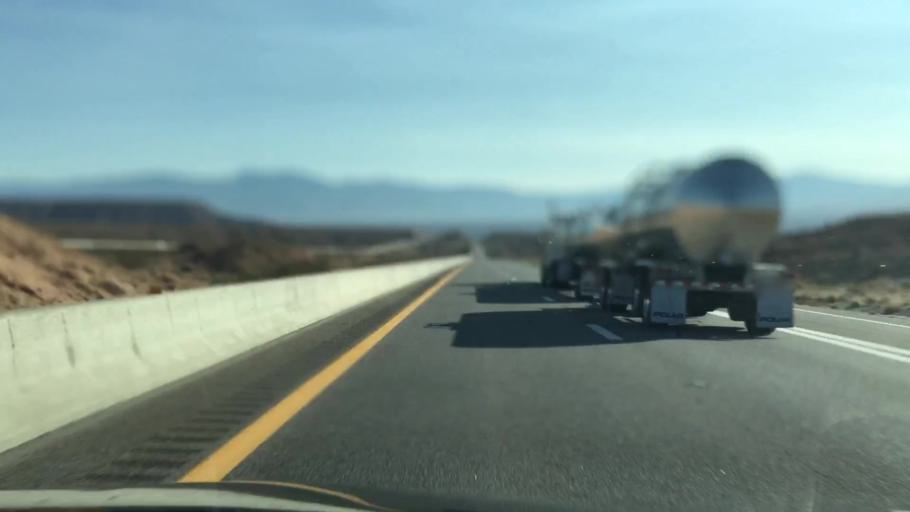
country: US
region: Nevada
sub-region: Clark County
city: Bunkerville
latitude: 36.7695
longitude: -114.2289
